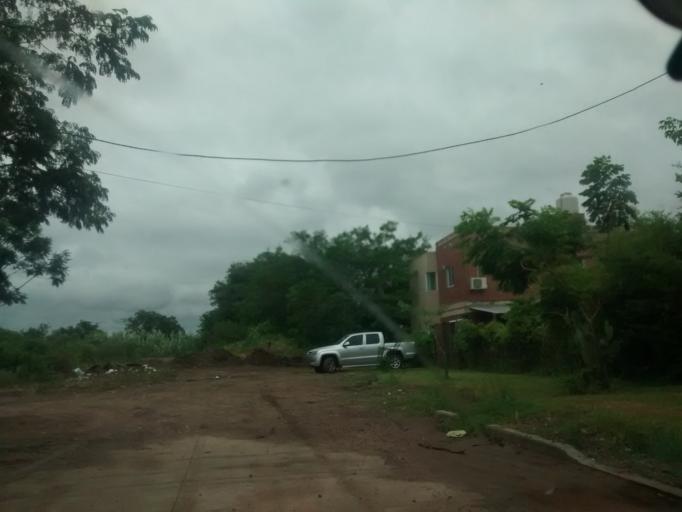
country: AR
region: Chaco
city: Resistencia
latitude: -27.4354
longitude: -58.9721
